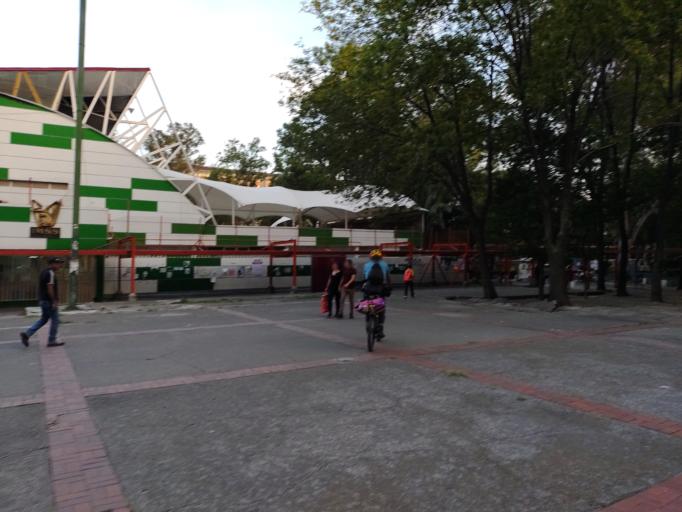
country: MX
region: Mexico City
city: Cuauhtemoc
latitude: 19.4542
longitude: -99.1435
